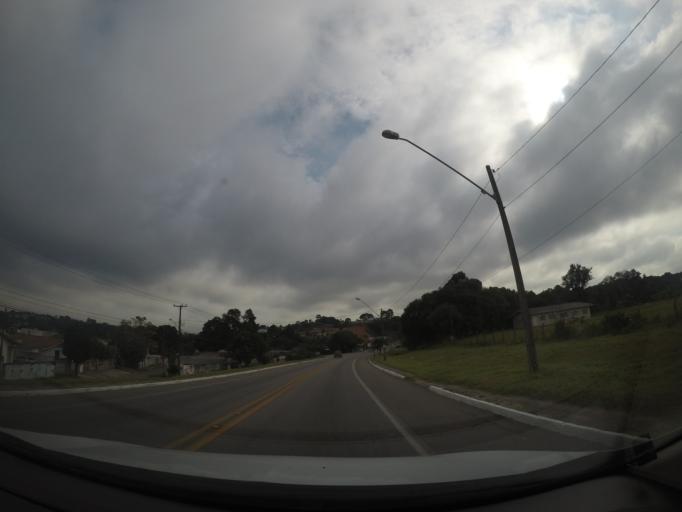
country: BR
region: Parana
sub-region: Colombo
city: Colombo
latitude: -25.3660
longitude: -49.2205
